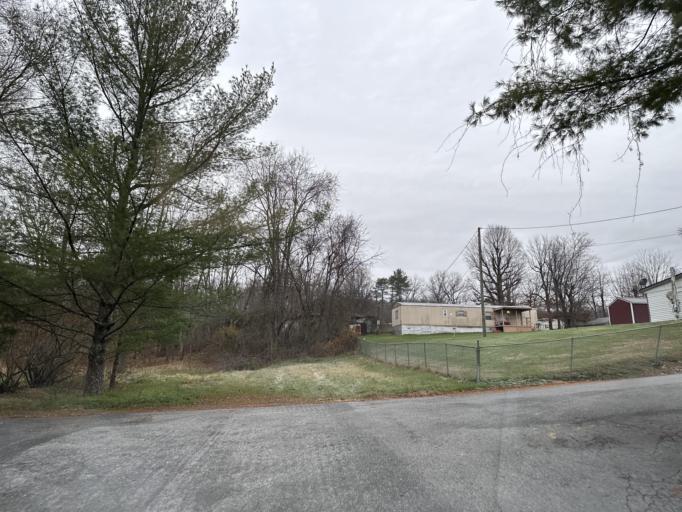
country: US
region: Virginia
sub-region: Rockbridge County
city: East Lexington
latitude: 38.0785
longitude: -79.3930
